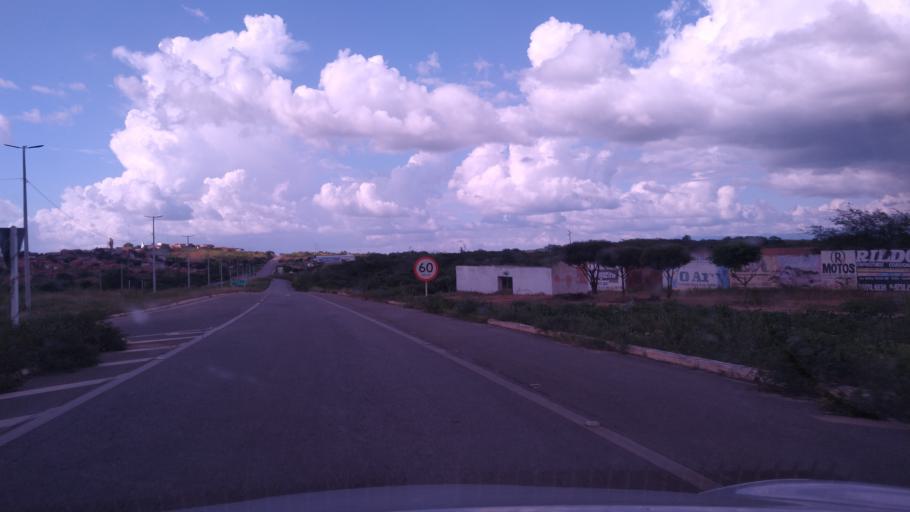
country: BR
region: Ceara
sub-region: Caninde
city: Caninde
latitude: -4.3794
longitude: -39.3093
